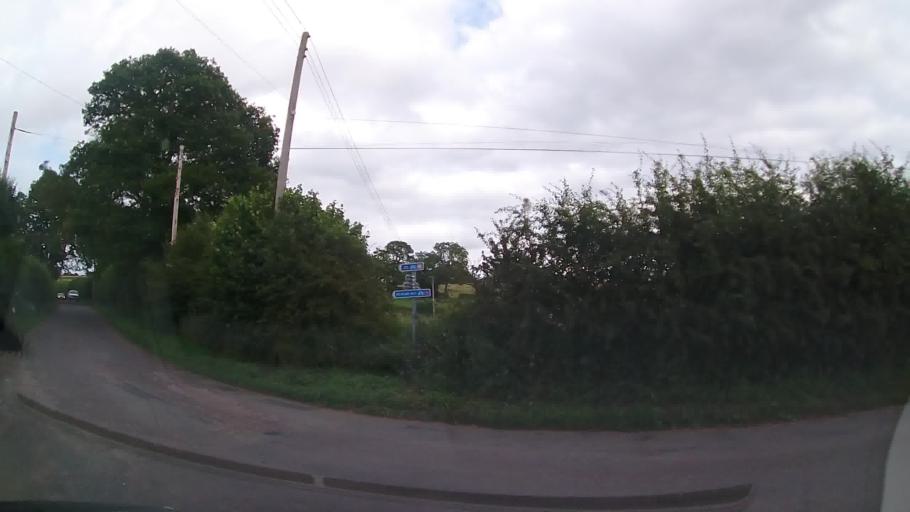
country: GB
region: England
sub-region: Shropshire
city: Whitchurch
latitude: 52.9347
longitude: -2.7243
